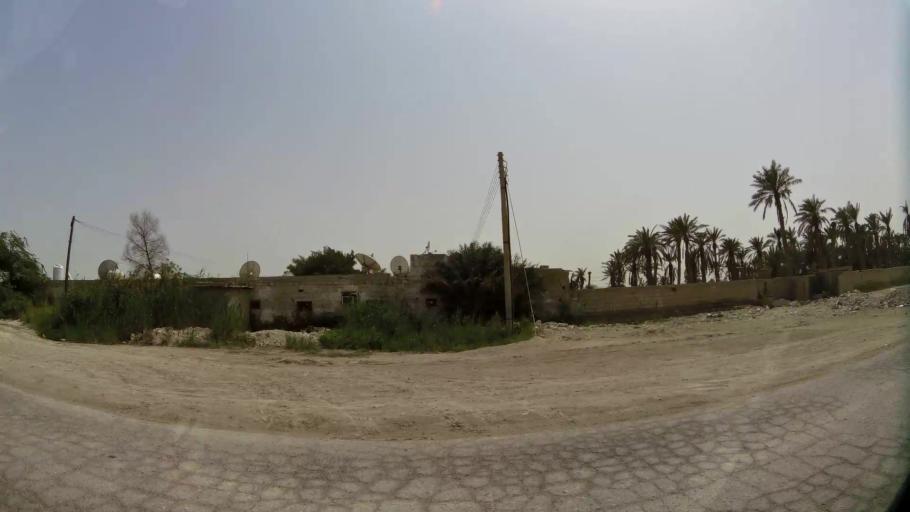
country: QA
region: Baladiyat ar Rayyan
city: Ar Rayyan
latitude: 25.2412
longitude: 51.4270
